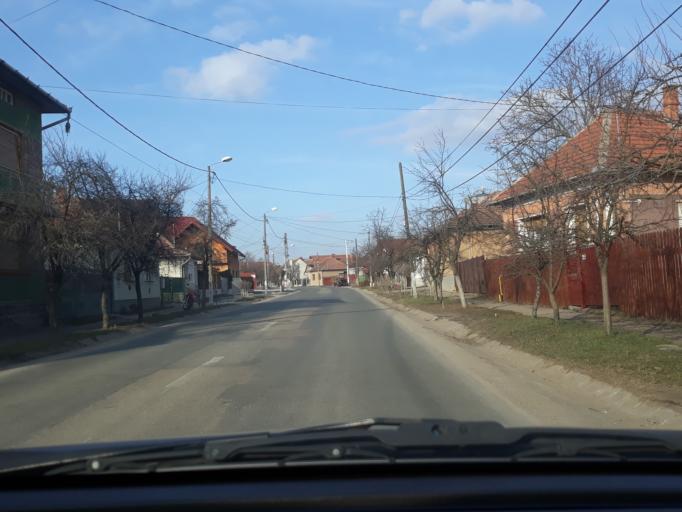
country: RO
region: Bihor
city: Margita
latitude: 47.3514
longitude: 22.3390
